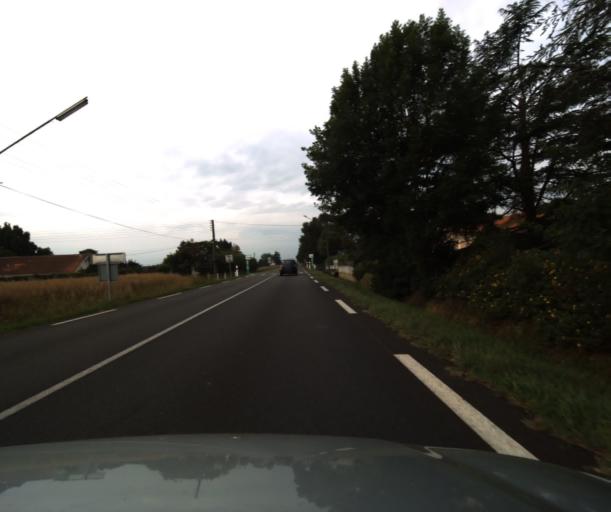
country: FR
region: Midi-Pyrenees
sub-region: Departement des Hautes-Pyrenees
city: Rabastens-de-Bigorre
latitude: 43.3797
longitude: 0.1479
